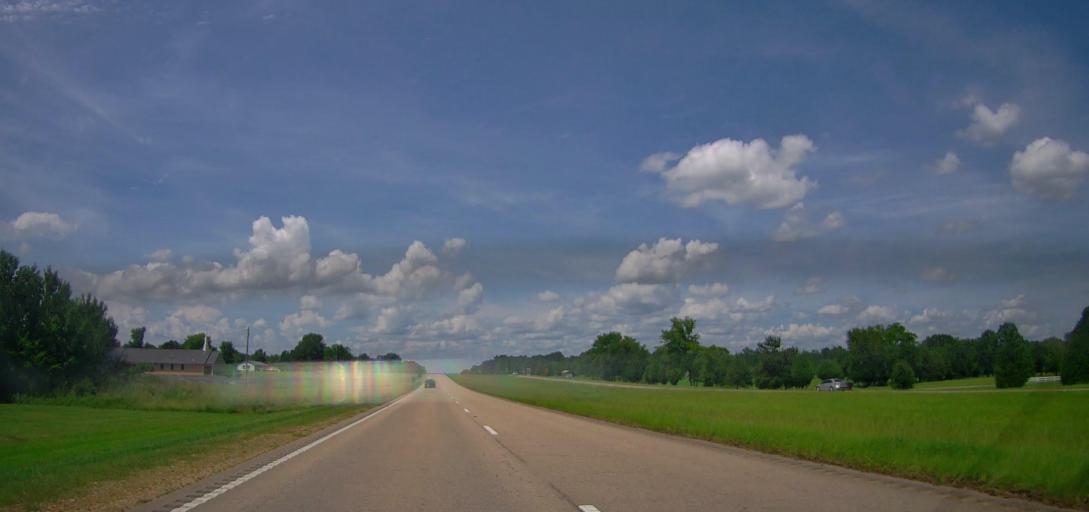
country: US
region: Mississippi
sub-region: Lee County
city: Nettleton
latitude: 34.0207
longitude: -88.6325
